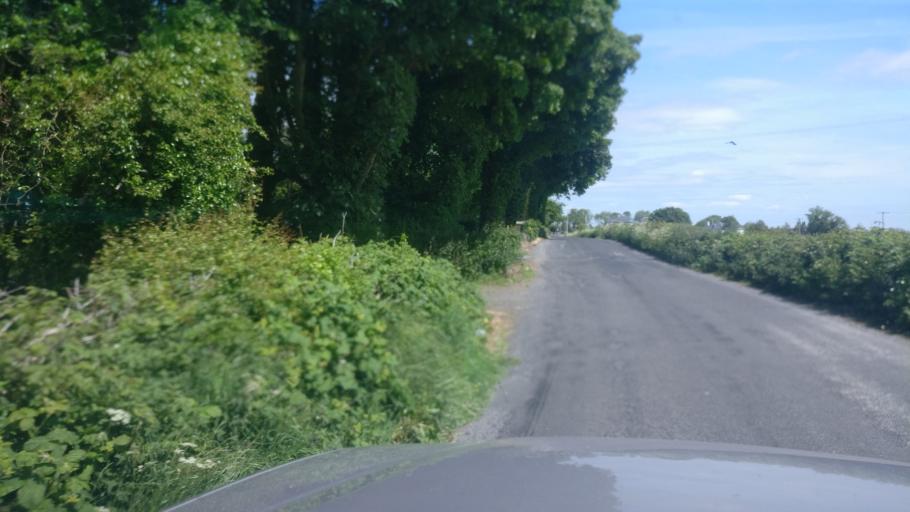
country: IE
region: Connaught
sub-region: County Galway
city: Gort
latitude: 53.1410
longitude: -8.7621
